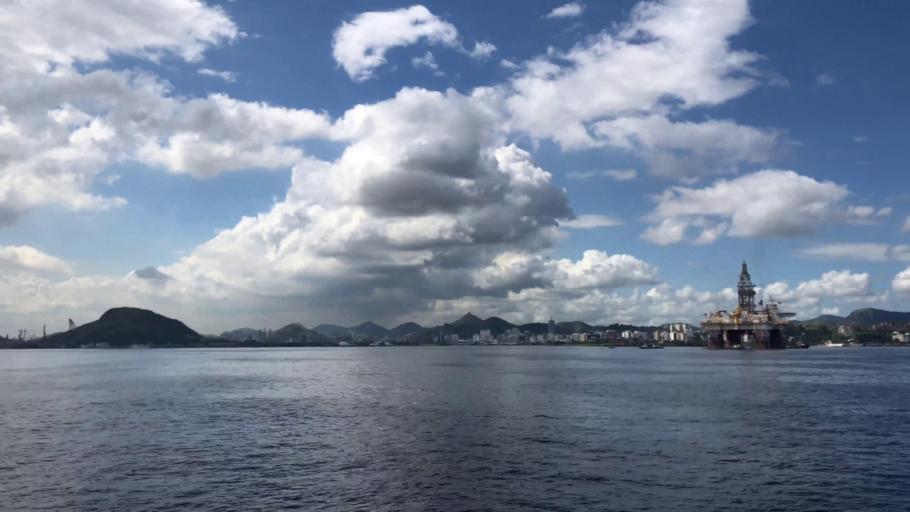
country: BR
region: Rio de Janeiro
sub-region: Niteroi
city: Niteroi
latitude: -22.8963
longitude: -43.1497
